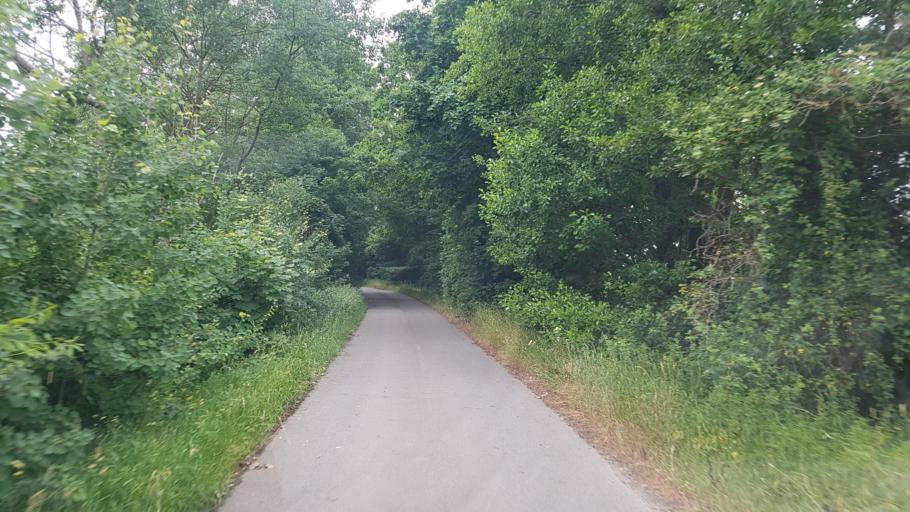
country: DE
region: Brandenburg
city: Grossthiemig
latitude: 51.4008
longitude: 13.6473
